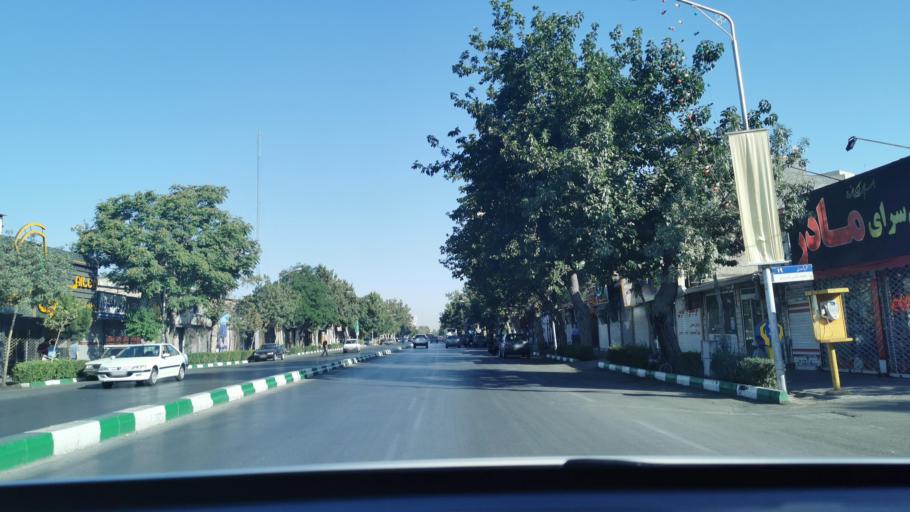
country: IR
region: Razavi Khorasan
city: Mashhad
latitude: 36.3103
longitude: 59.5928
